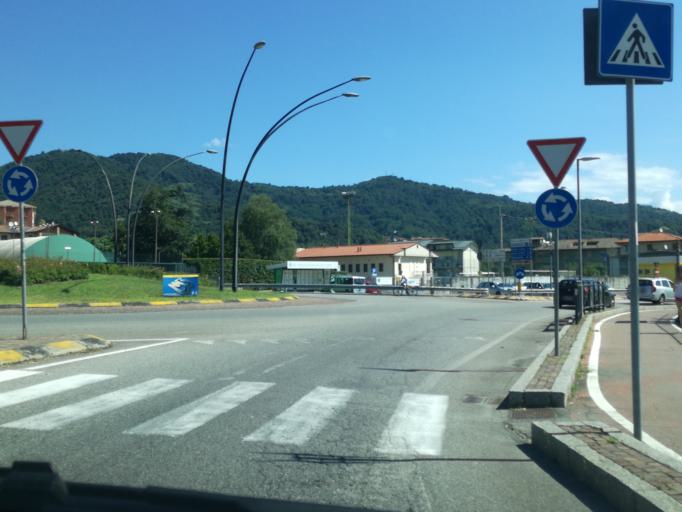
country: IT
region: Lombardy
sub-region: Provincia di Bergamo
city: Carvico
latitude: 45.7006
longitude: 9.4799
